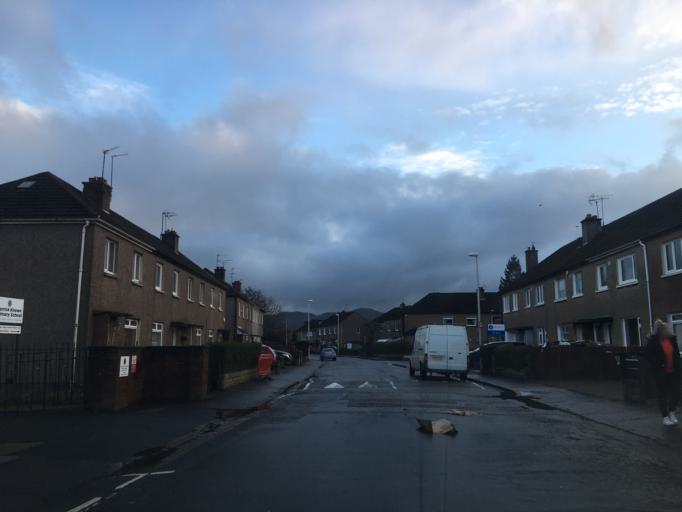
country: GB
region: Scotland
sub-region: Edinburgh
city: Colinton
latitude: 55.9386
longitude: -3.2758
